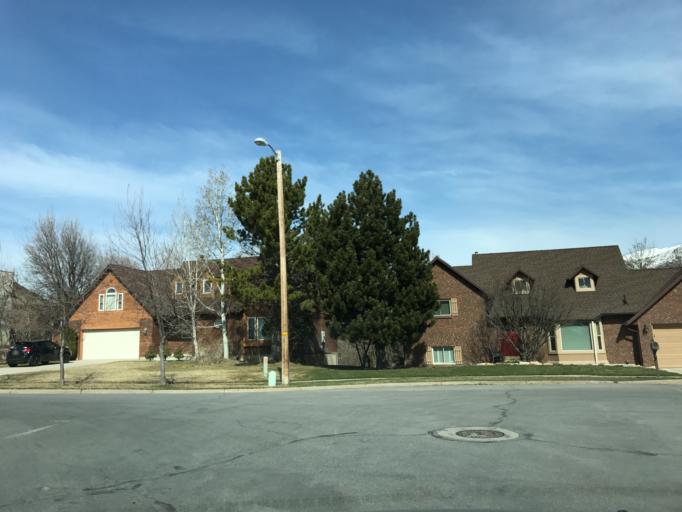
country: US
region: Utah
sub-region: Davis County
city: South Weber
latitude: 41.1129
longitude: -111.9113
